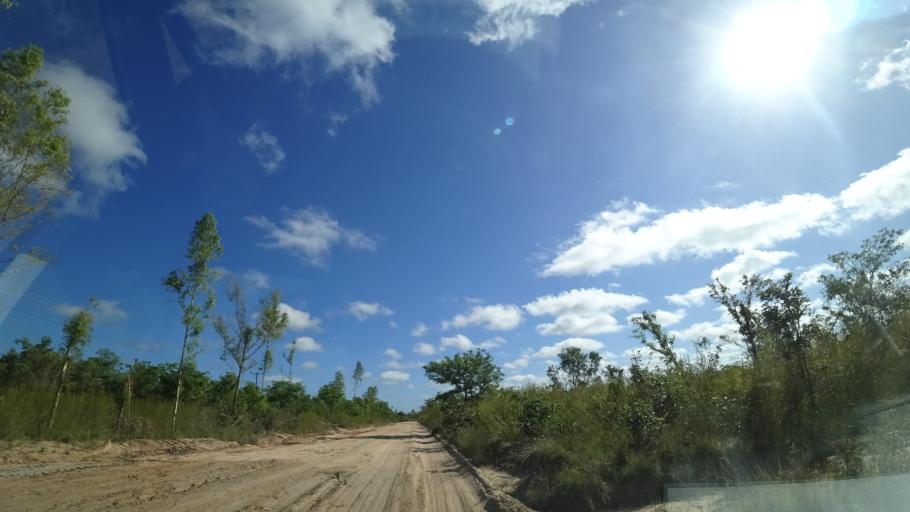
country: MZ
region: Sofala
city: Dondo
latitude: -19.4398
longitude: 34.7144
